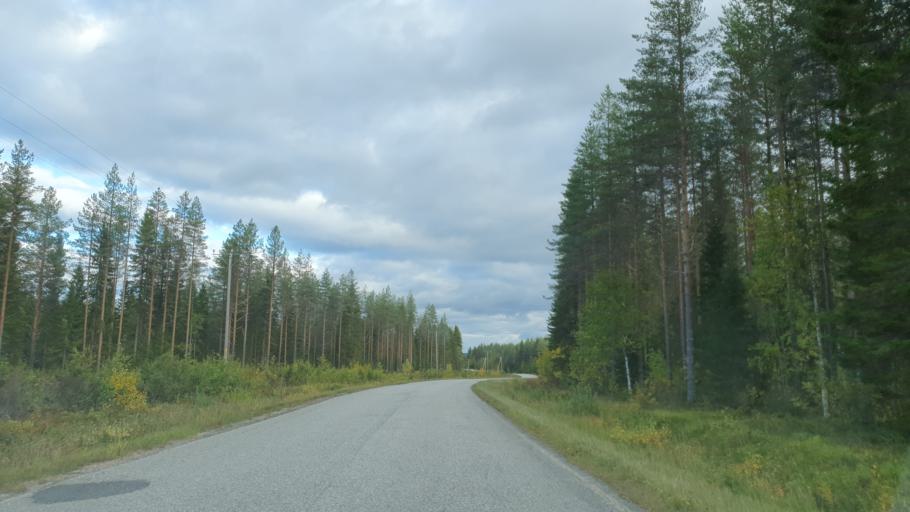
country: FI
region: Kainuu
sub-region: Kehys-Kainuu
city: Kuhmo
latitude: 63.9506
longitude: 29.8612
